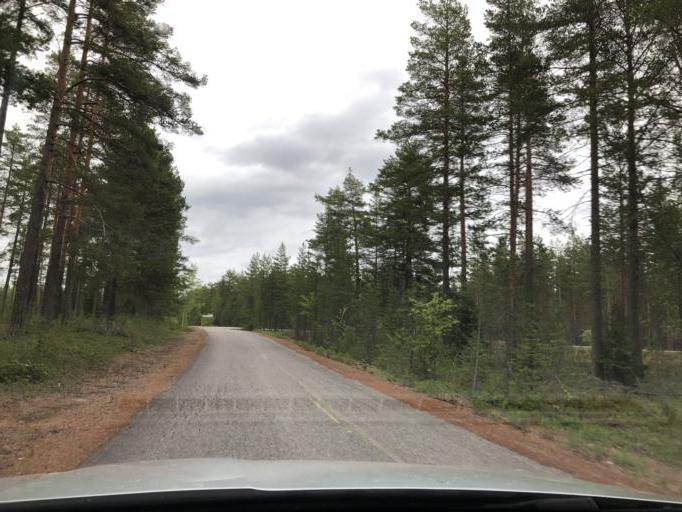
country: SE
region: Norrbotten
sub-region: Pitea Kommun
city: Pitea
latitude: 65.2373
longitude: 21.5180
